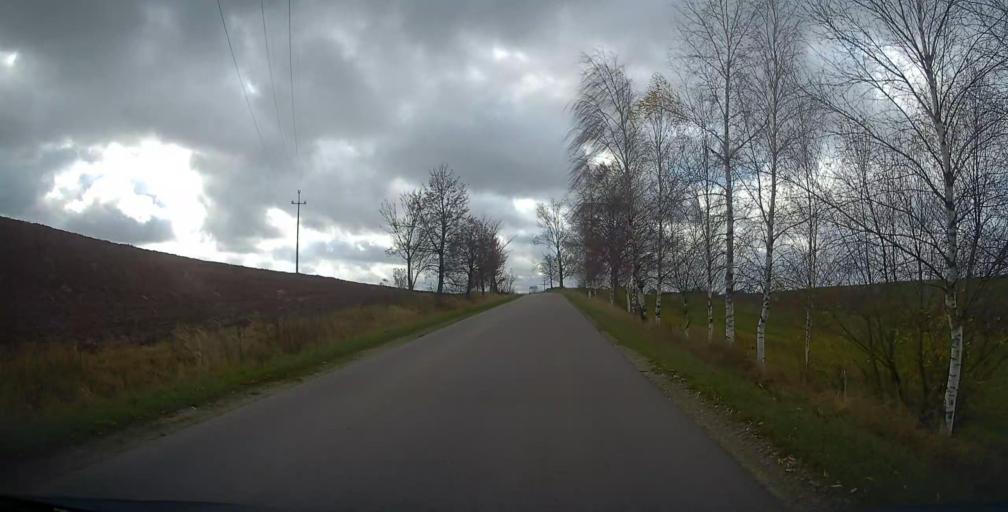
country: PL
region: Podlasie
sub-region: Suwalki
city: Suwalki
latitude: 54.3613
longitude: 22.8569
